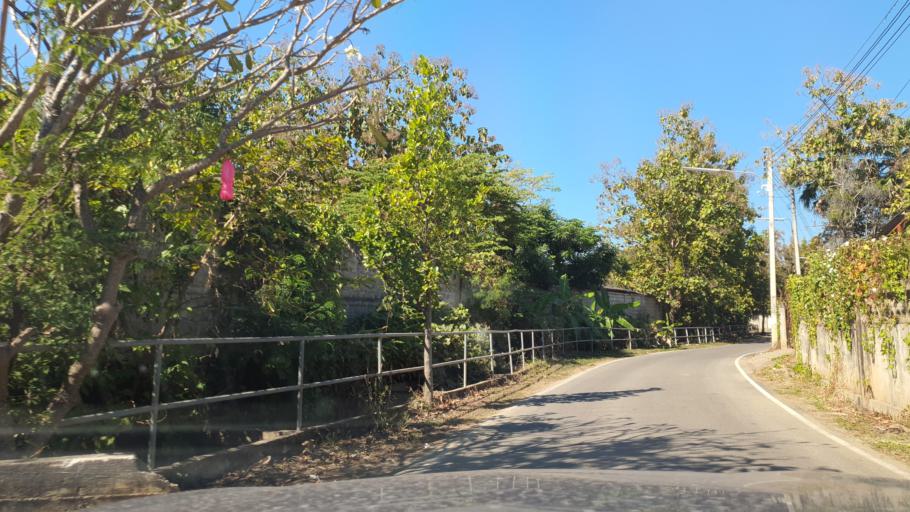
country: TH
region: Chiang Mai
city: Hang Dong
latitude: 18.6790
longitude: 98.9277
